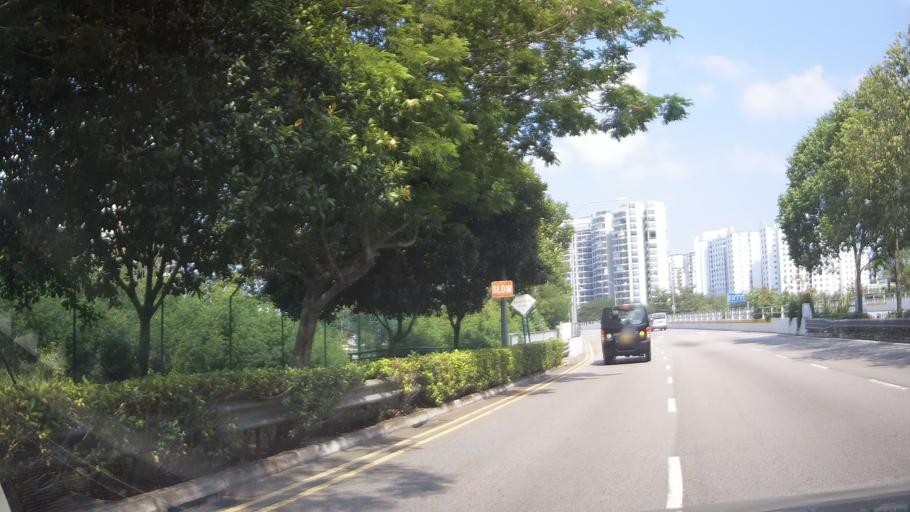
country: MY
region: Johor
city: Kampung Pasir Gudang Baru
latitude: 1.3799
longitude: 103.9060
